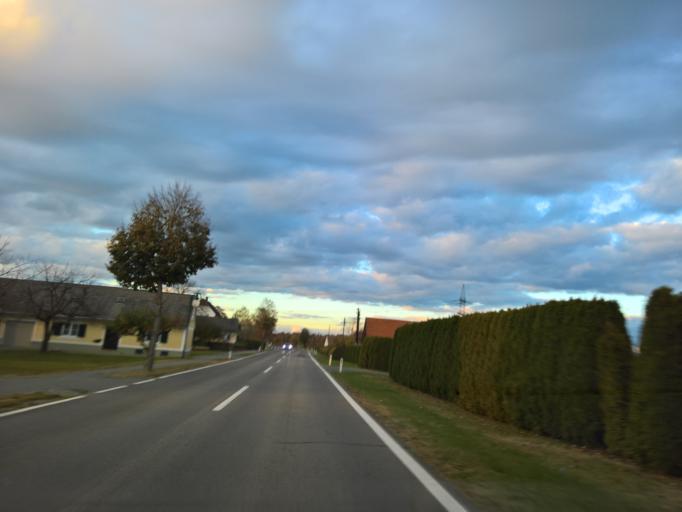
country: AT
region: Styria
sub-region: Politischer Bezirk Leibnitz
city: Lang
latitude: 46.8334
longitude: 15.5429
